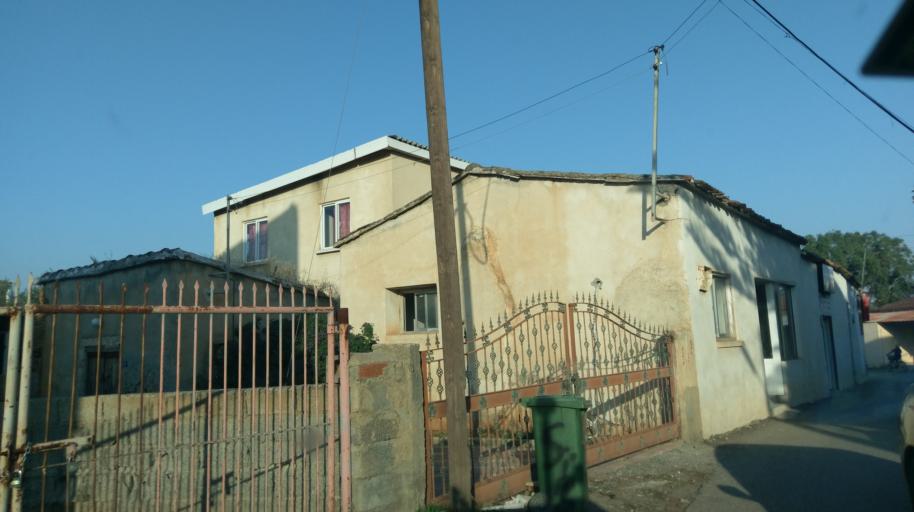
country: CY
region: Lefkosia
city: Lefka
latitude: 35.1328
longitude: 32.9122
